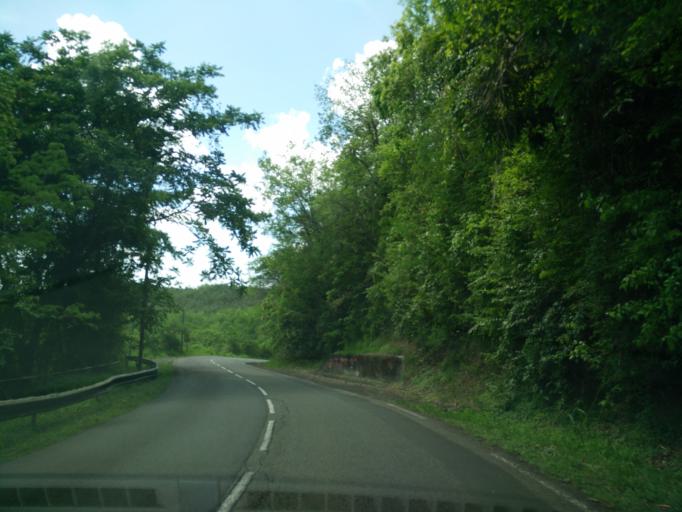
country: MQ
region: Martinique
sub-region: Martinique
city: Les Trois-Ilets
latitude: 14.5359
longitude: -61.0544
